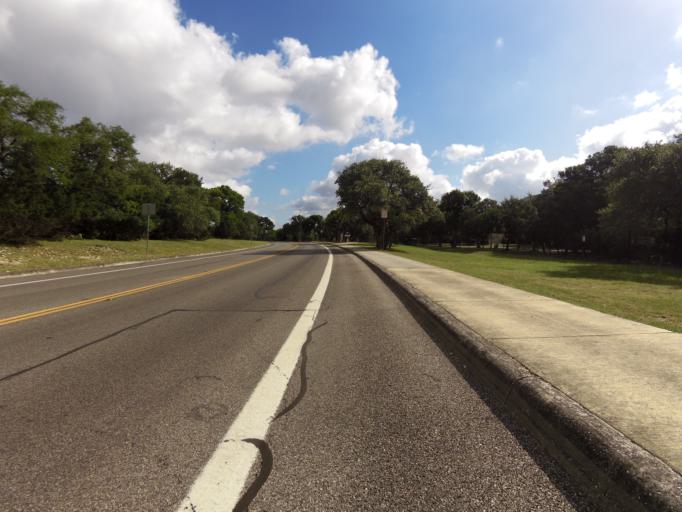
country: US
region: Texas
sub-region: Bexar County
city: Shavano Park
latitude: 29.5836
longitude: -98.6072
